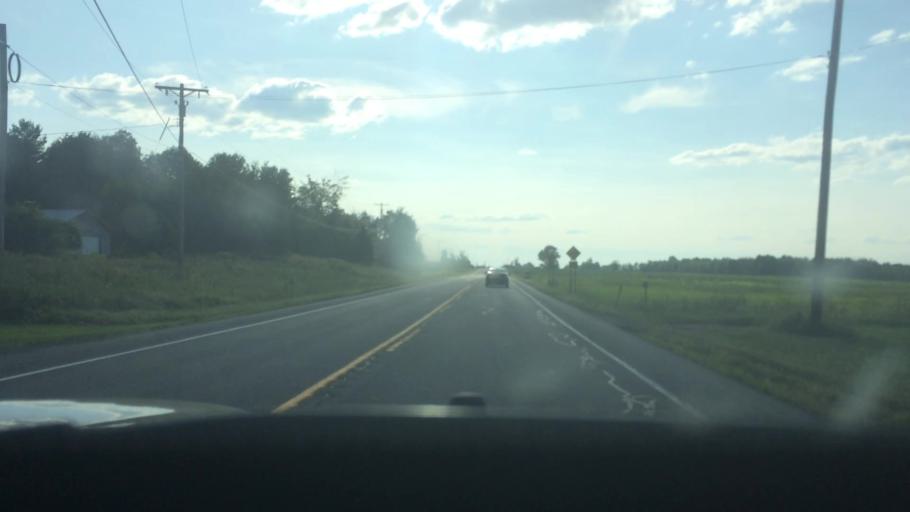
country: US
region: New York
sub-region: St. Lawrence County
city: Potsdam
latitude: 44.6896
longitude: -74.7475
